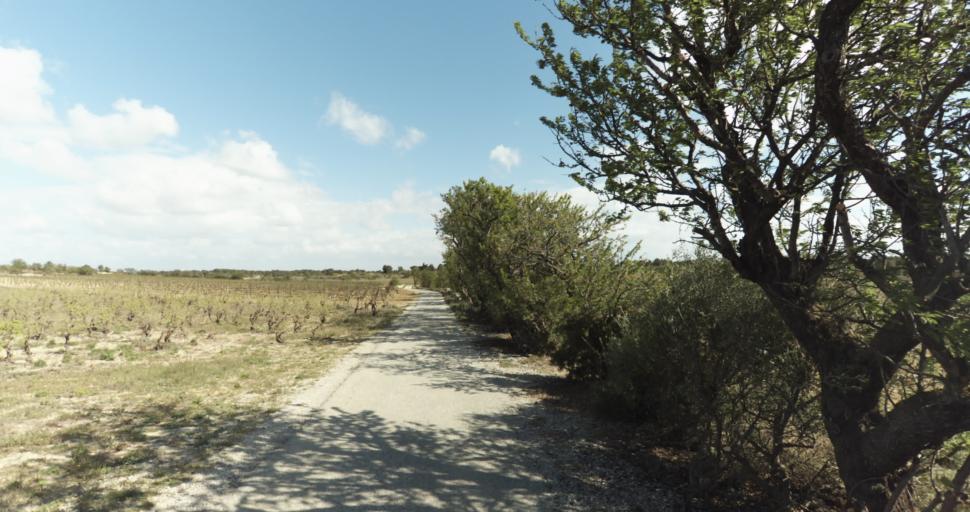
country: FR
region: Languedoc-Roussillon
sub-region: Departement de l'Aude
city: Leucate
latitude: 42.9219
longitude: 3.0365
